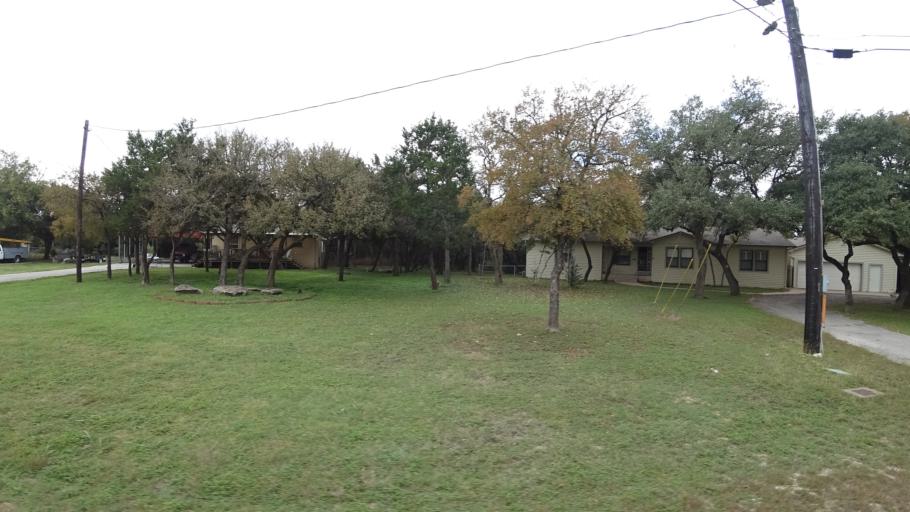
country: US
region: Texas
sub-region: Travis County
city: Bee Cave
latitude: 30.2520
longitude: -97.9219
